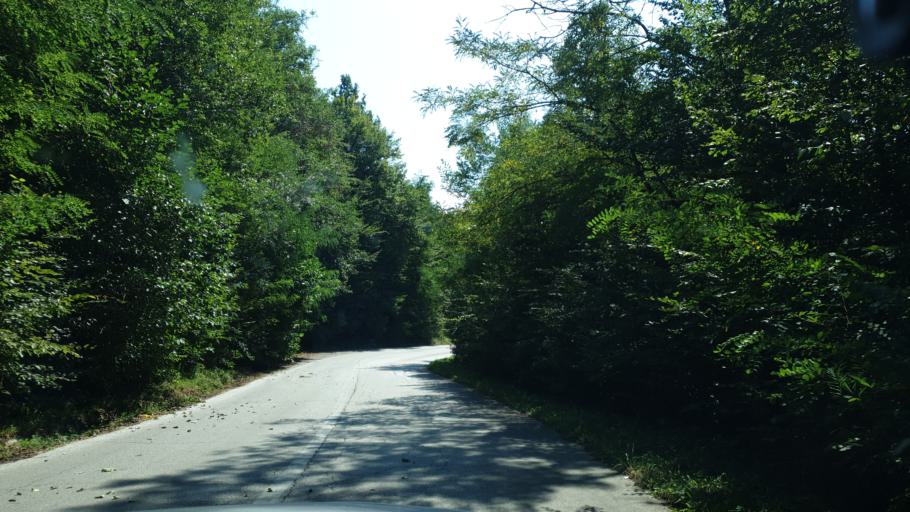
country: RS
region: Central Serbia
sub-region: Zlatiborski Okrug
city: Cajetina
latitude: 43.6730
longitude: 19.8267
